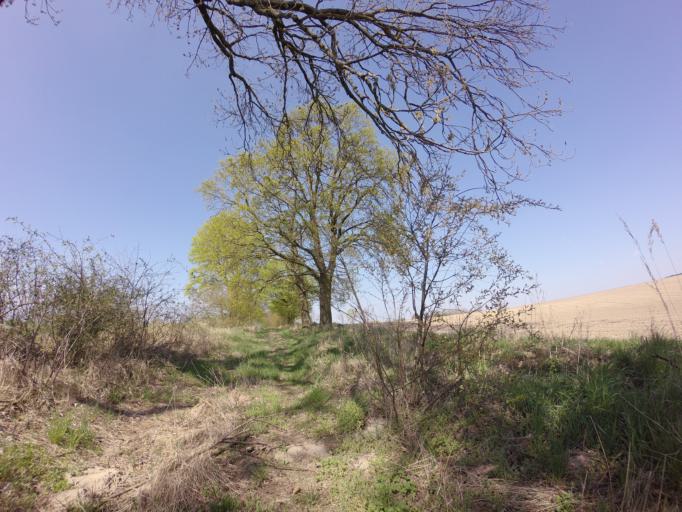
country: PL
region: West Pomeranian Voivodeship
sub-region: Powiat choszczenski
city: Choszczno
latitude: 53.2013
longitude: 15.3689
